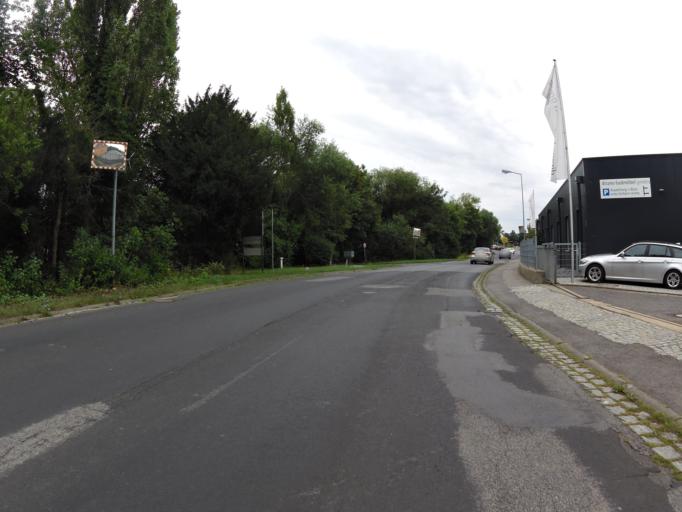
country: DE
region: Bavaria
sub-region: Regierungsbezirk Unterfranken
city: Zeil
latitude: 50.0051
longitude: 10.5934
